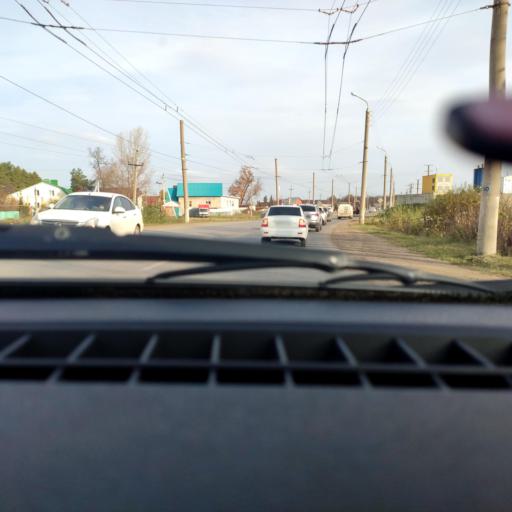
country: RU
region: Bashkortostan
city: Ufa
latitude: 54.7821
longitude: 55.9476
